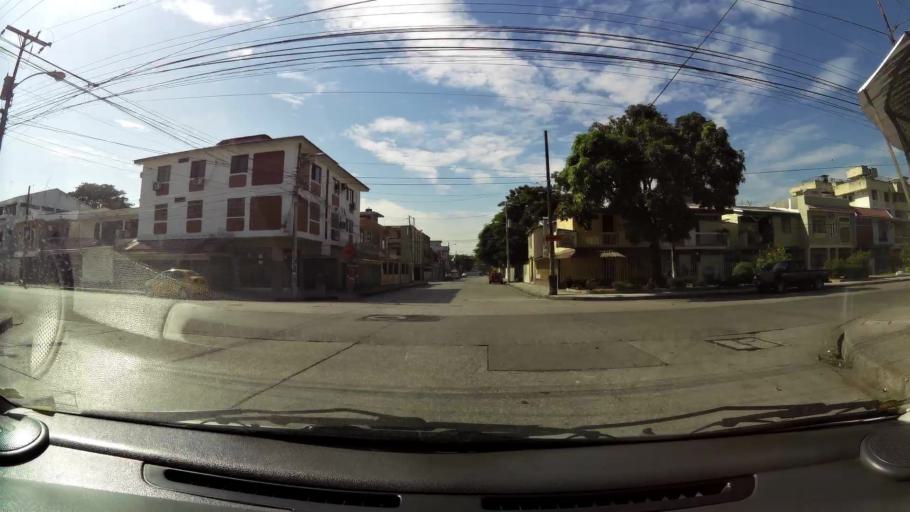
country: EC
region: Guayas
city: Guayaquil
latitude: -2.2289
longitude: -79.8918
